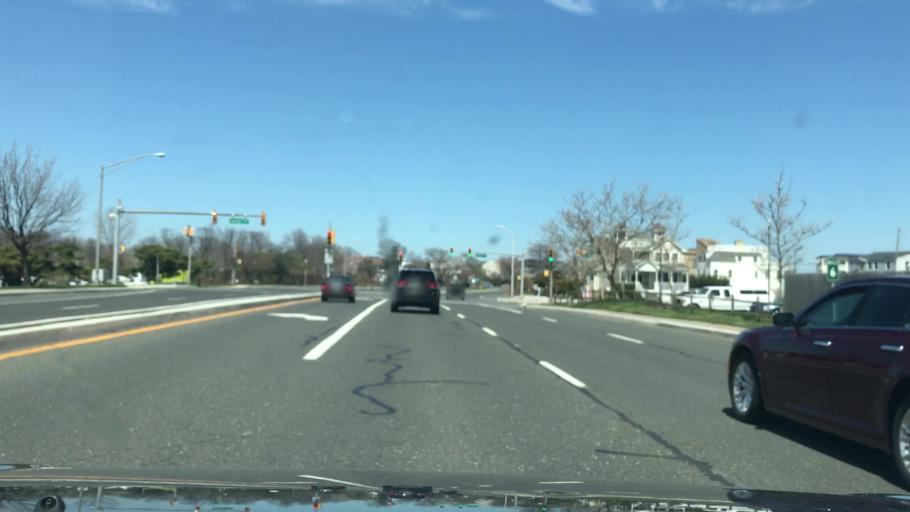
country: US
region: New Jersey
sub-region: Monmouth County
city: Monmouth Beach
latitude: 40.3171
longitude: -73.9796
